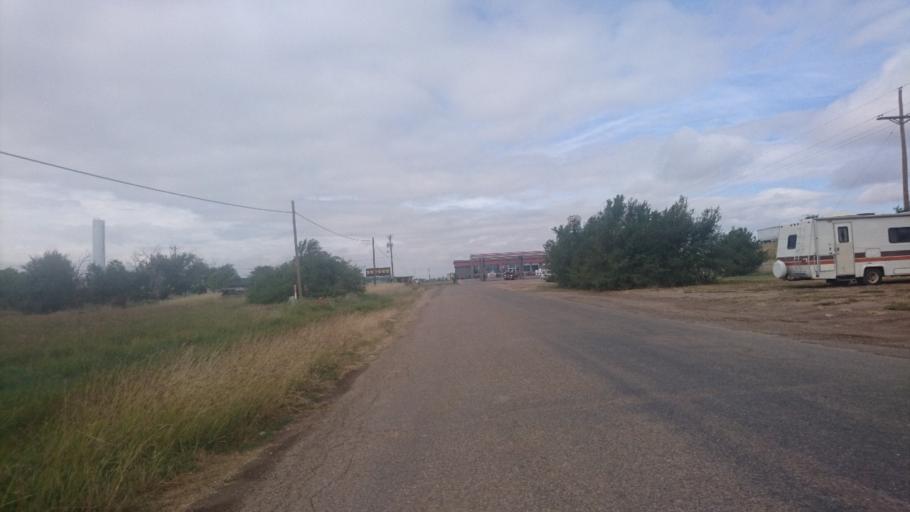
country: US
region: Texas
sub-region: Potter County
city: Bushland
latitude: 35.1905
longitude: -102.0641
